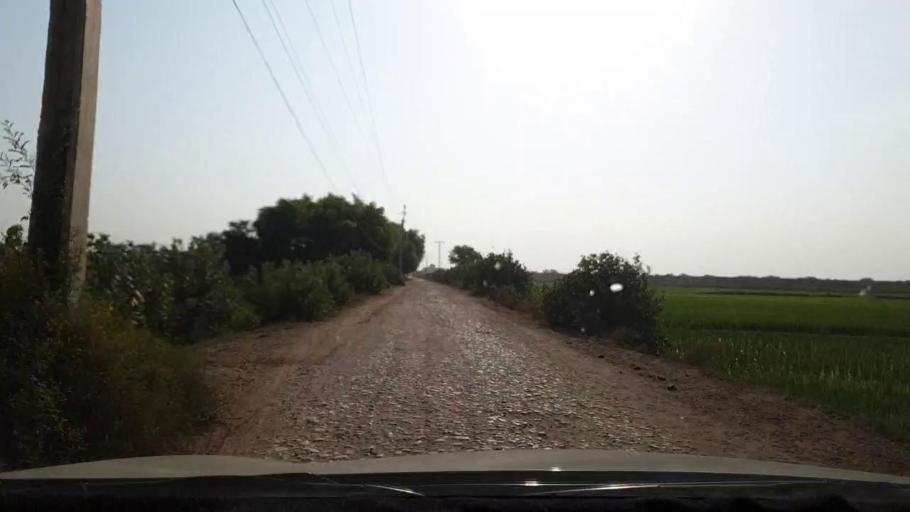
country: PK
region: Sindh
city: Larkana
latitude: 27.5534
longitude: 68.2692
